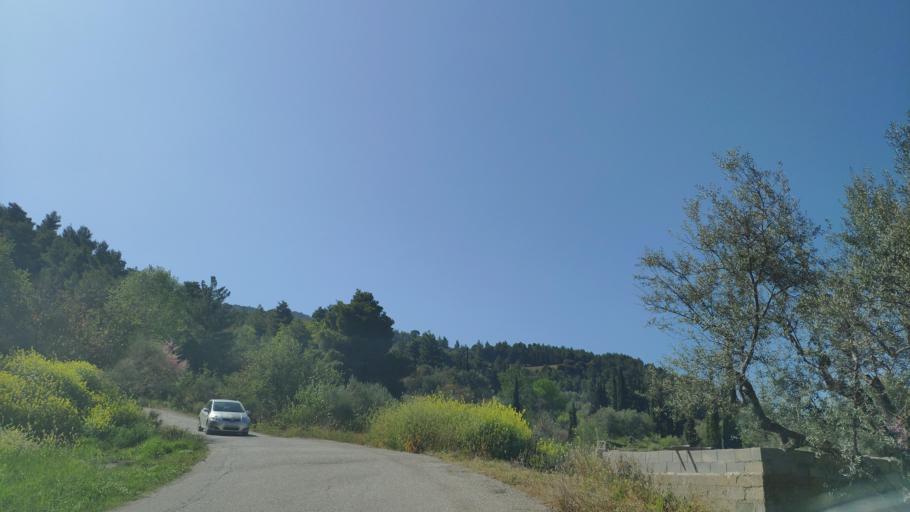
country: GR
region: West Greece
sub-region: Nomos Achaias
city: Aiyira
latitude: 38.0830
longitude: 22.3359
